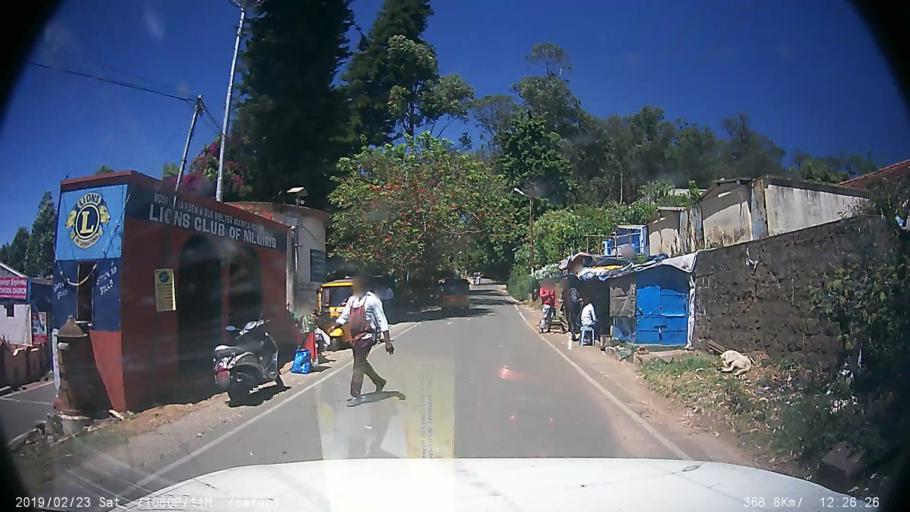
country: IN
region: Tamil Nadu
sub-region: Nilgiri
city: Wellington
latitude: 11.3439
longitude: 76.7879
